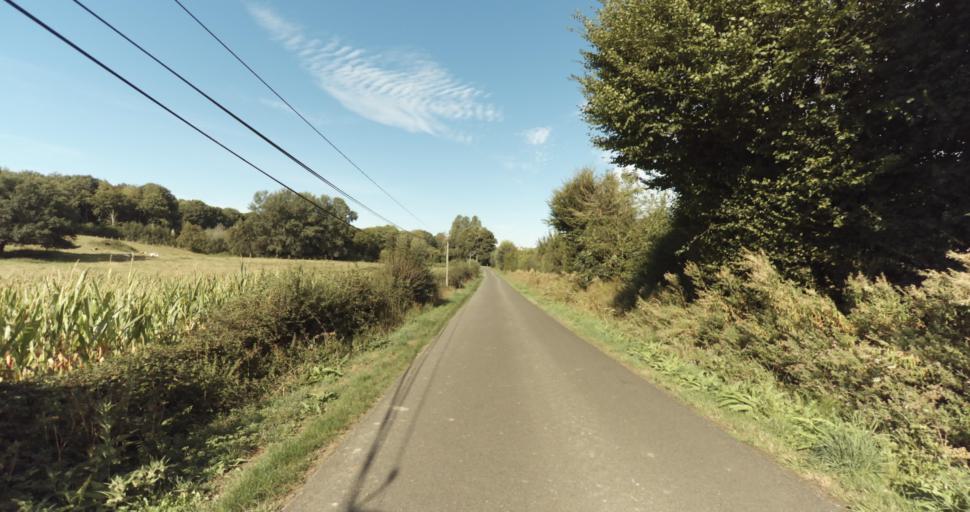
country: FR
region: Lower Normandy
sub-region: Departement de l'Orne
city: Gace
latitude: 48.8137
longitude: 0.2176
